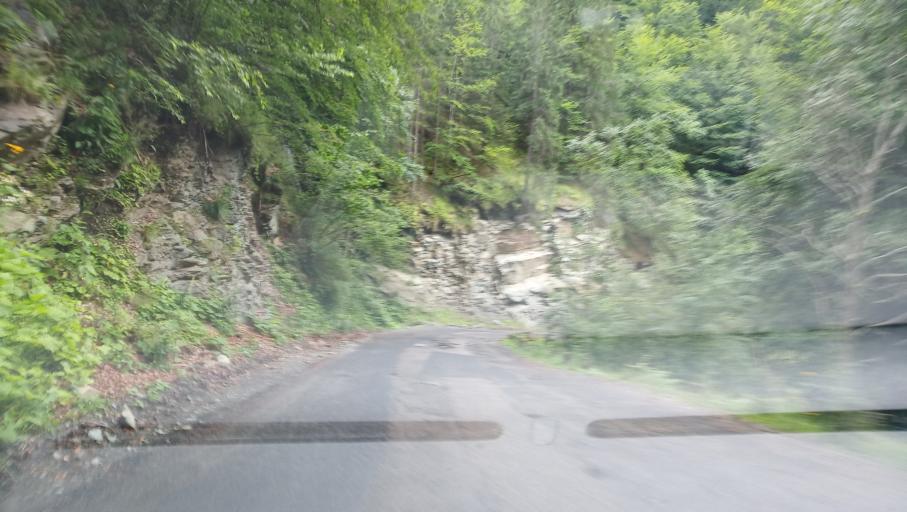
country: RO
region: Hunedoara
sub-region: Oras Petrila
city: Petrila
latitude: 45.4123
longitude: 23.4671
